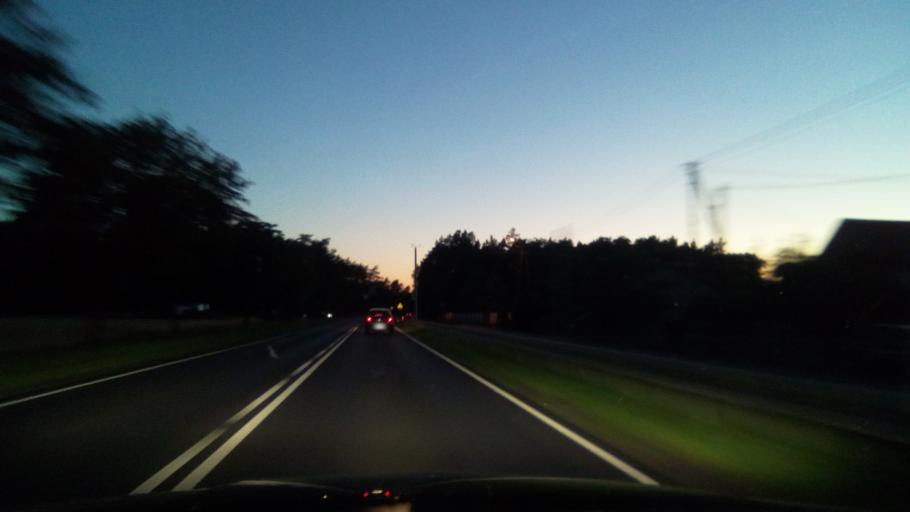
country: PL
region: Greater Poland Voivodeship
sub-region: Powiat slupecki
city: Ladek
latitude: 52.2480
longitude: 18.0067
